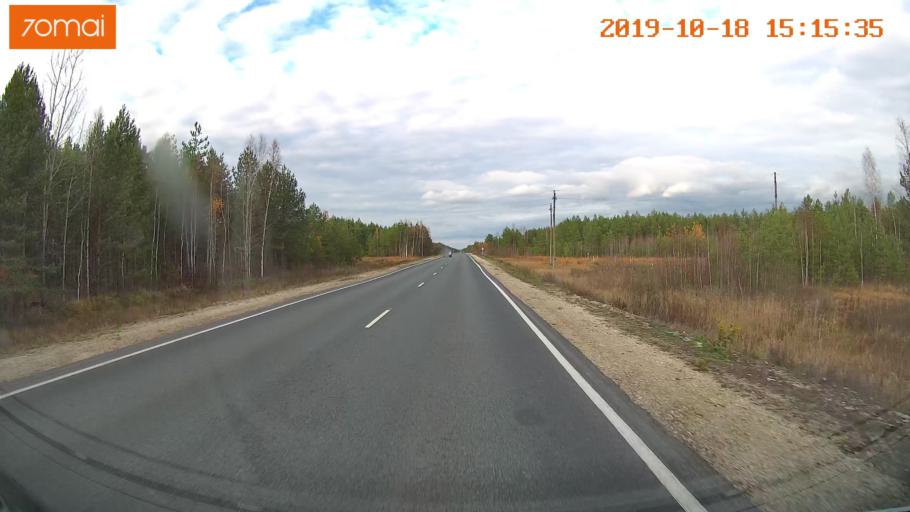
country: RU
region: Vladimir
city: Gus'-Khrustal'nyy
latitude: 55.6215
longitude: 40.7229
